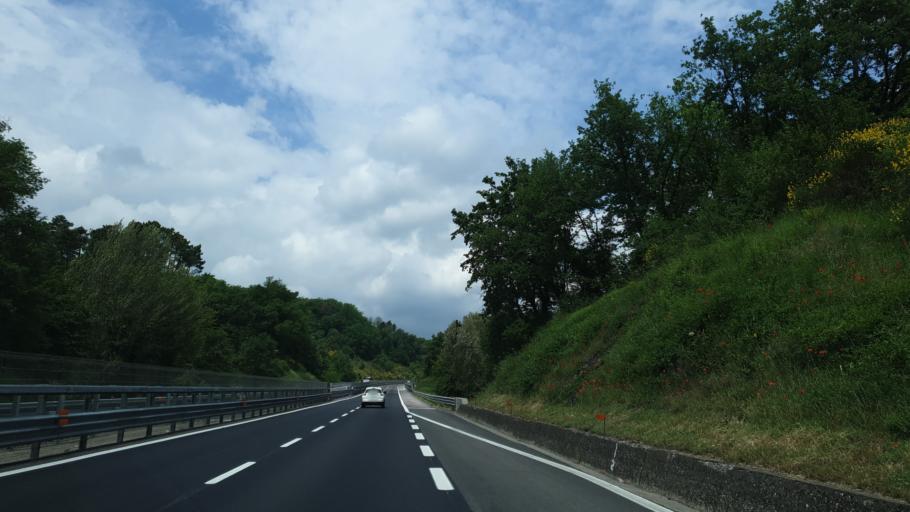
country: IT
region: Tuscany
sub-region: Province of Florence
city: Barberino di Mugello
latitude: 43.9975
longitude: 11.2200
